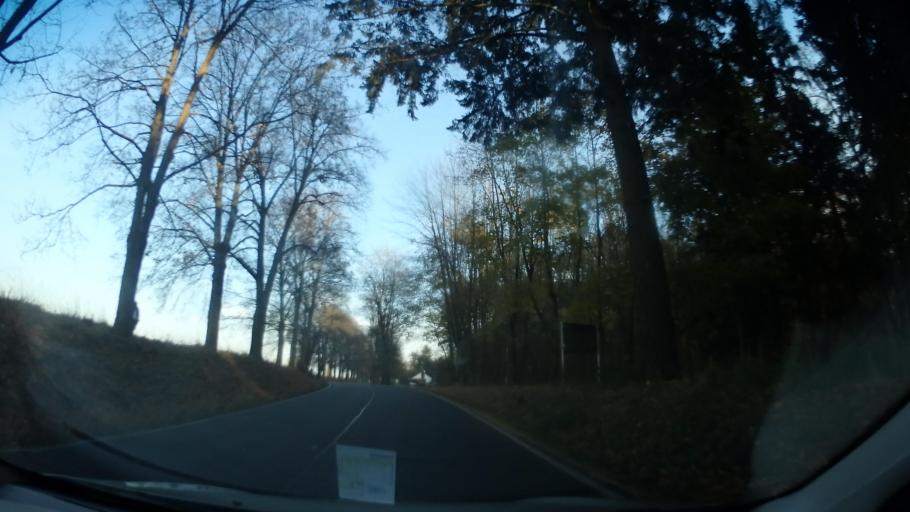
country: CZ
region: Central Bohemia
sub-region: Okres Benesov
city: Benesov
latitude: 49.7809
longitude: 14.6687
